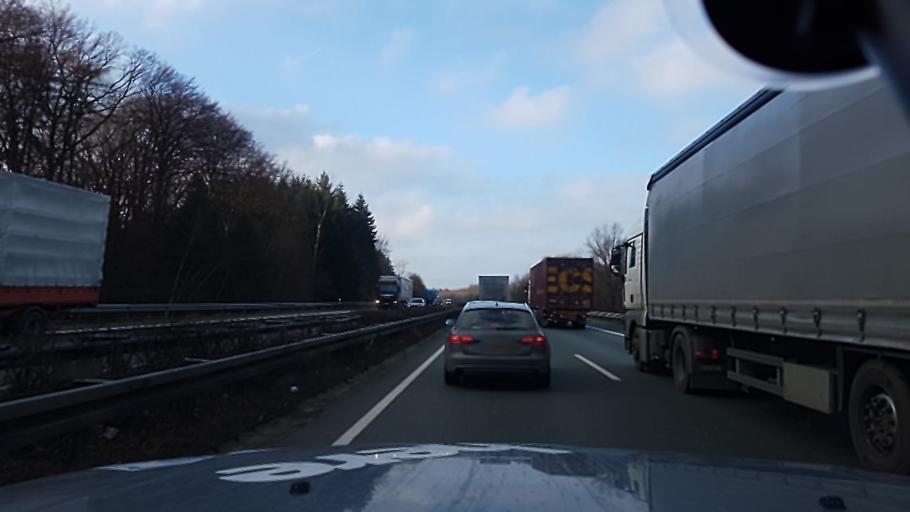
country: DE
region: North Rhine-Westphalia
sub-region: Regierungsbezirk Munster
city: Birgte
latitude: 52.2829
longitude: 7.6318
